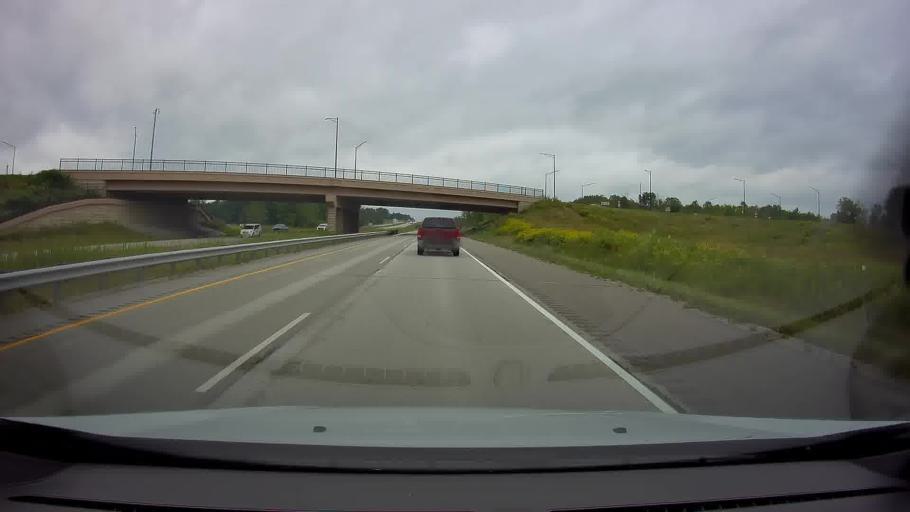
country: US
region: Wisconsin
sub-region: Brown County
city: Howard
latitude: 44.5602
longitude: -88.1293
